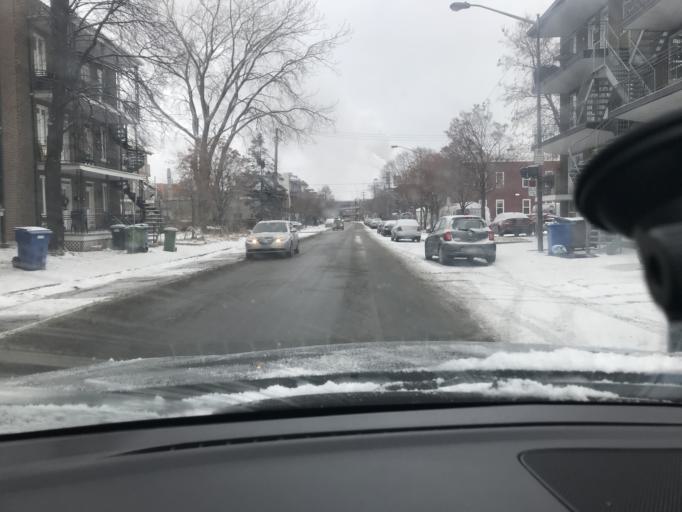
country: CA
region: Quebec
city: Quebec
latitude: 46.8211
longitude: -71.2234
